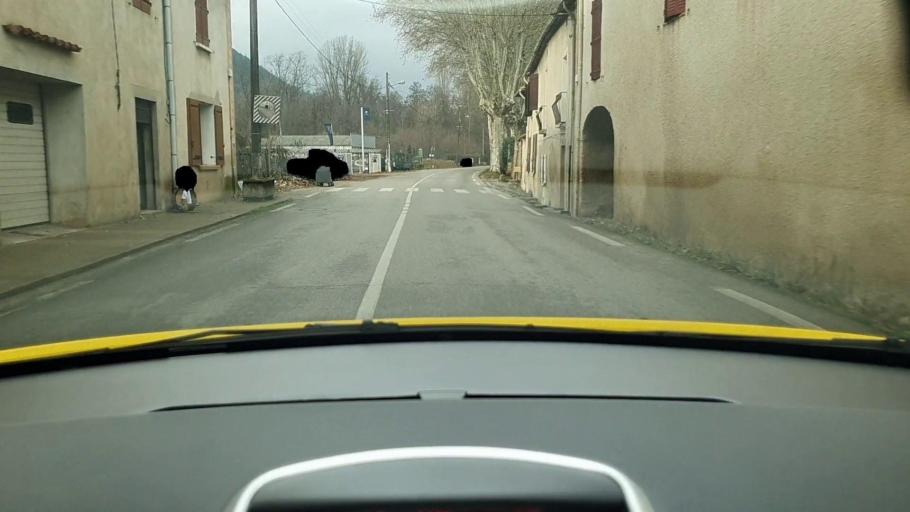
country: FR
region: Languedoc-Roussillon
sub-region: Departement du Gard
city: Besseges
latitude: 44.2849
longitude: 4.1143
